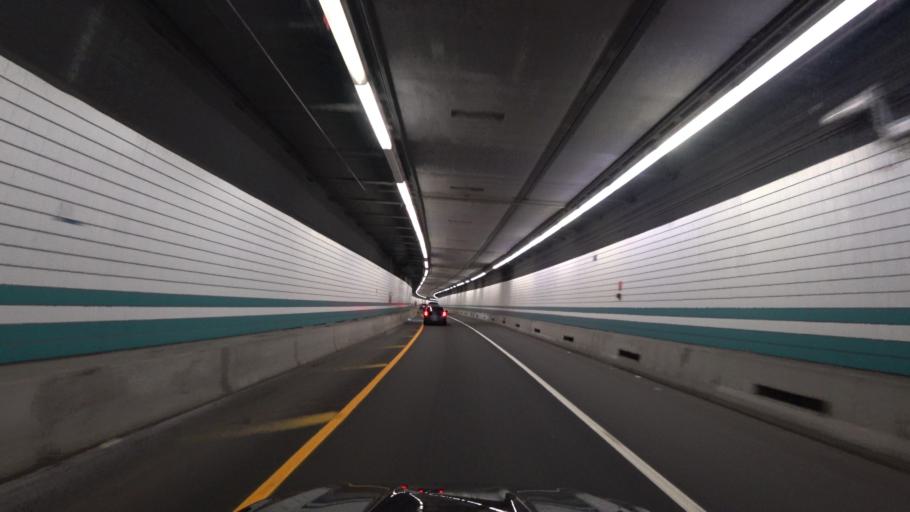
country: US
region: Massachusetts
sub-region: Suffolk County
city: South Boston
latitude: 42.3463
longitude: -71.0479
